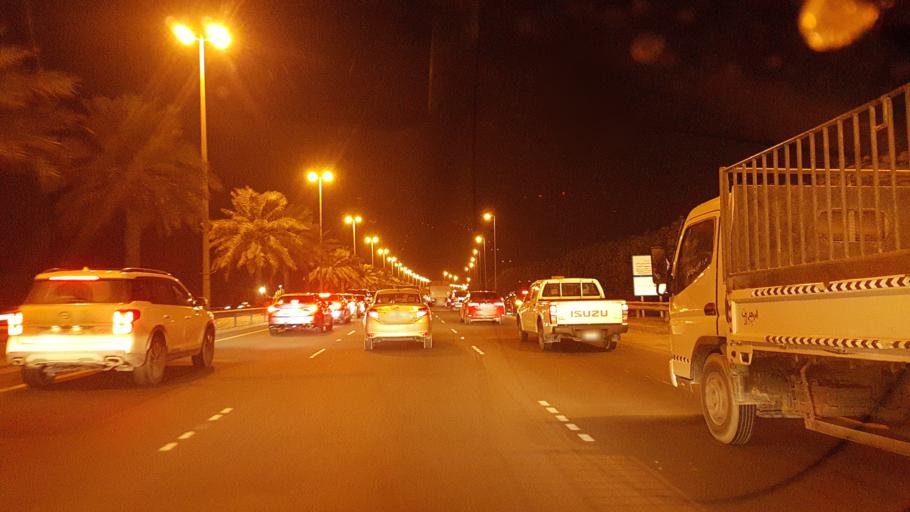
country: BH
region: Central Governorate
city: Madinat Hamad
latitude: 26.1592
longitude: 50.5053
